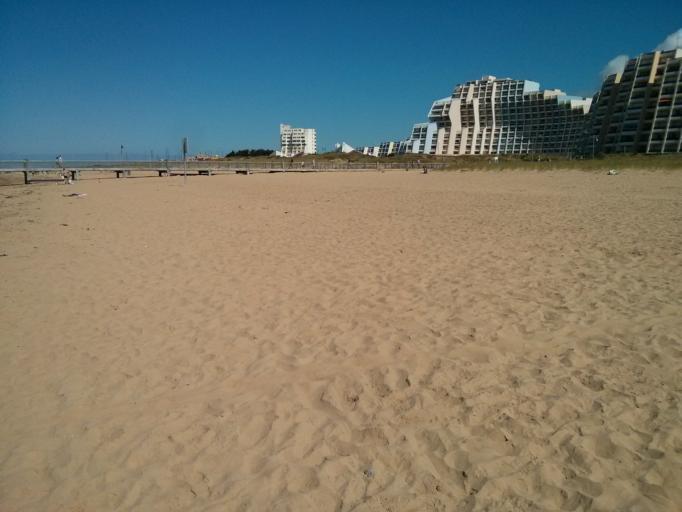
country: FR
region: Pays de la Loire
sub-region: Departement de la Vendee
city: Saint-Jean-de-Monts
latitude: 46.7865
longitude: -2.0821
